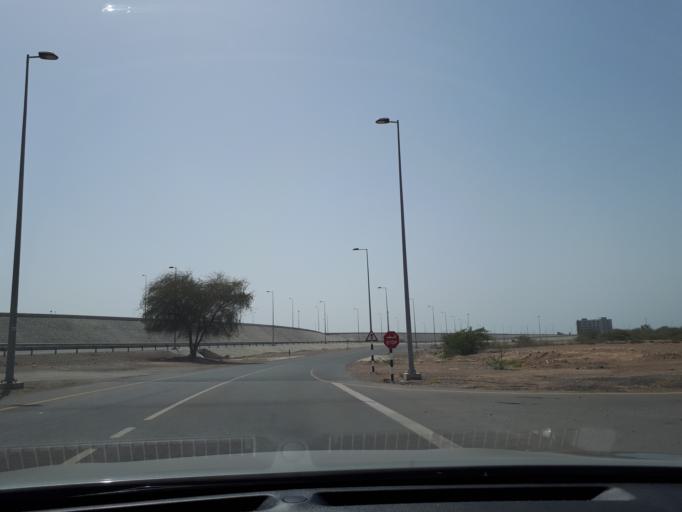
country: OM
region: Al Batinah
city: Barka'
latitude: 23.6878
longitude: 58.0283
